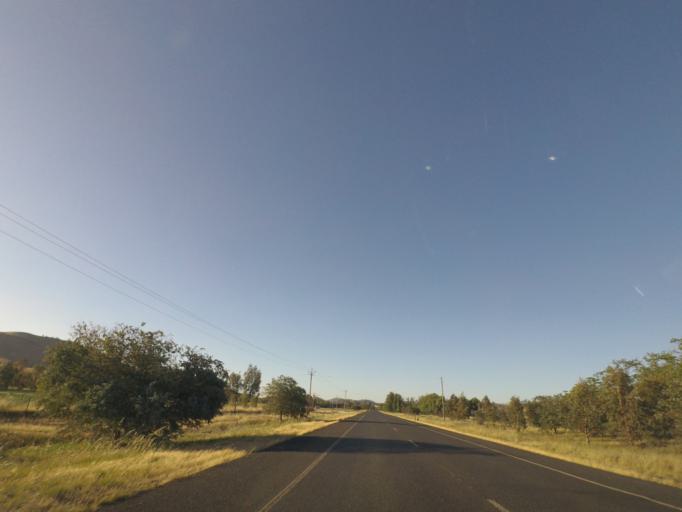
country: AU
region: New South Wales
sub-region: Gundagai
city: Gundagai
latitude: -34.9403
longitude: 148.1680
